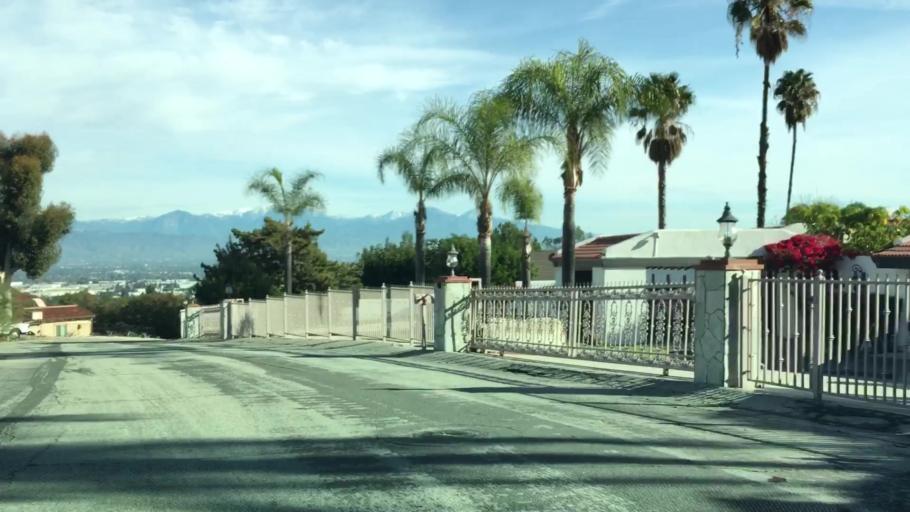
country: US
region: California
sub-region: Los Angeles County
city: Hacienda Heights
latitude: 34.0087
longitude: -117.9865
